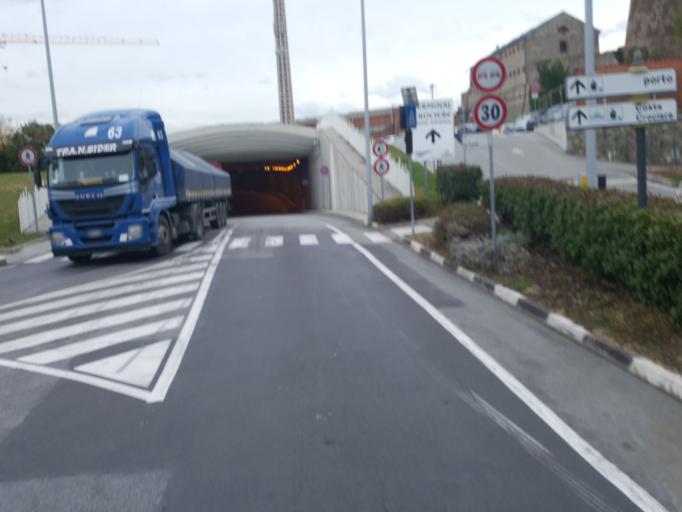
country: IT
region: Liguria
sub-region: Provincia di Savona
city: Savona
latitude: 44.3059
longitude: 8.4841
